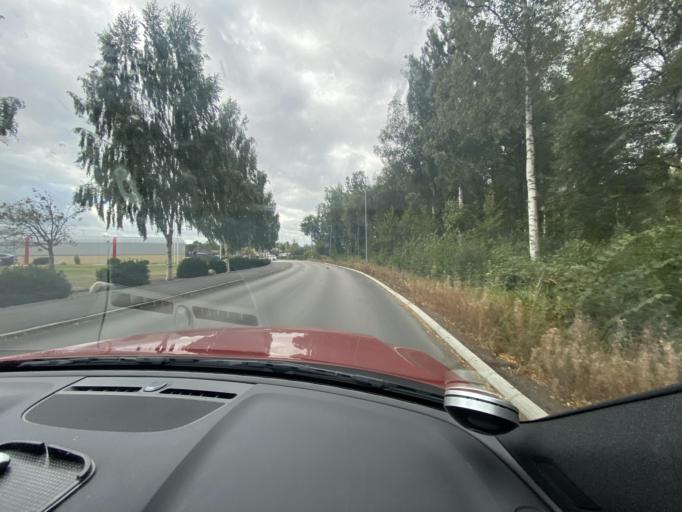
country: SE
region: Kronoberg
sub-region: Markaryds Kommun
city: Markaryd
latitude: 56.4499
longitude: 13.6008
